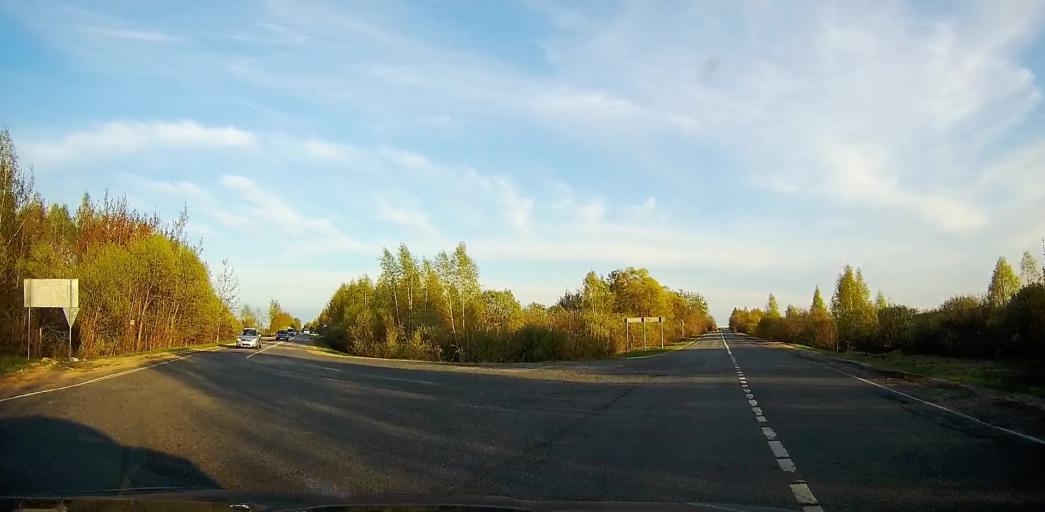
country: RU
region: Moskovskaya
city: Bronnitsy
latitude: 55.2786
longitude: 38.2189
